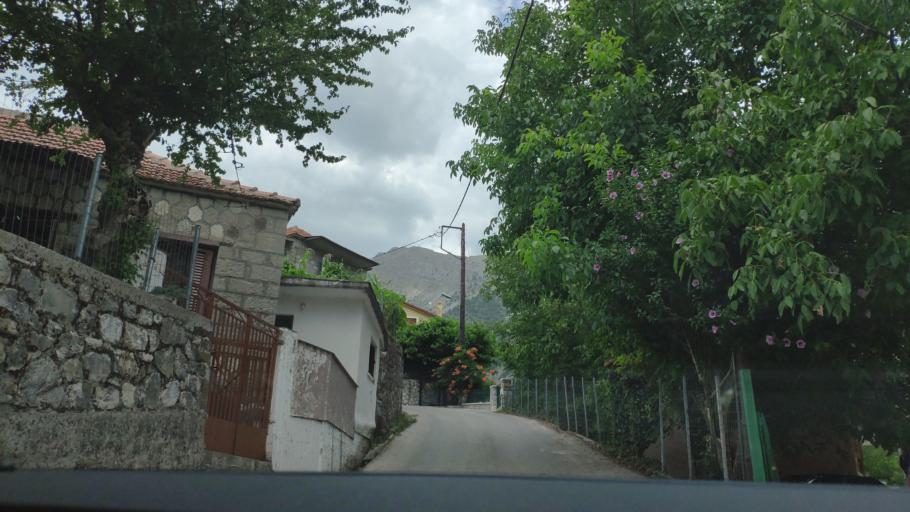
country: GR
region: Epirus
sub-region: Nomos Artas
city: Voulgareli
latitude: 39.4359
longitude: 21.2101
